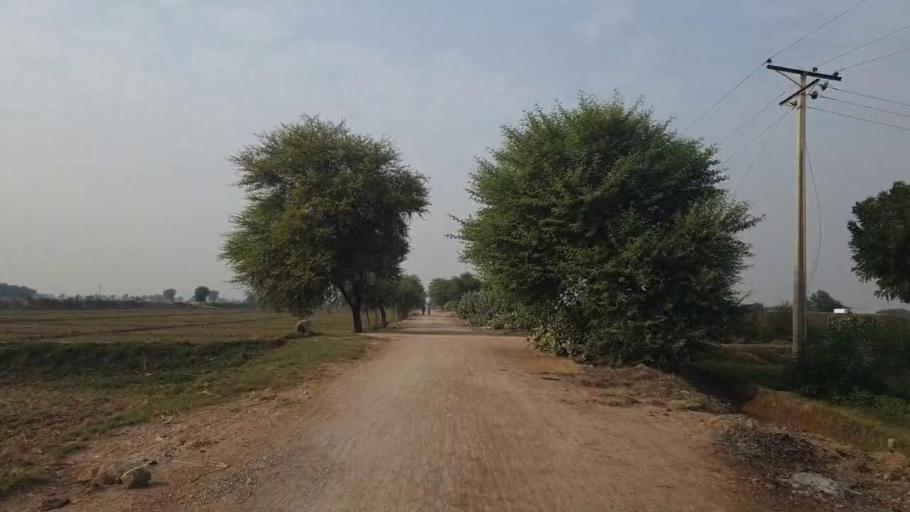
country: PK
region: Sindh
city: Sann
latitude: 26.0617
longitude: 68.1207
